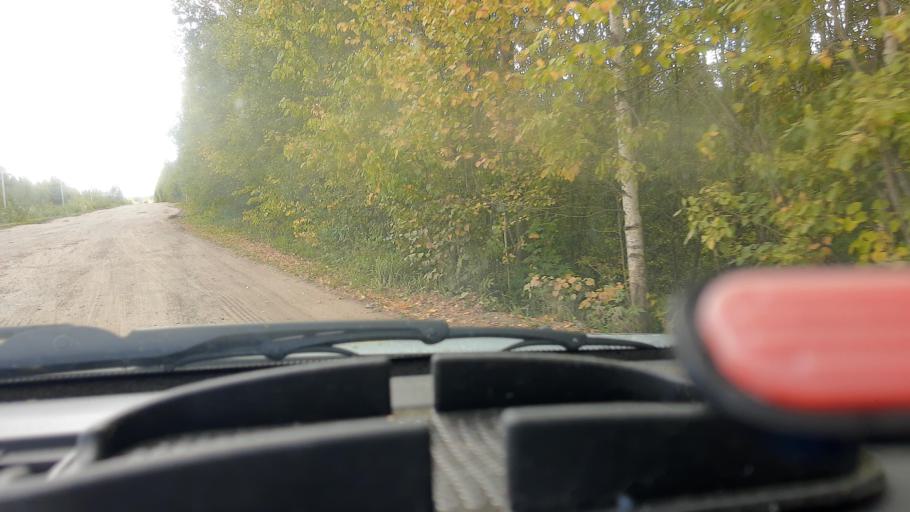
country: RU
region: Mariy-El
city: Kilemary
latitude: 56.8941
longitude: 46.7515
